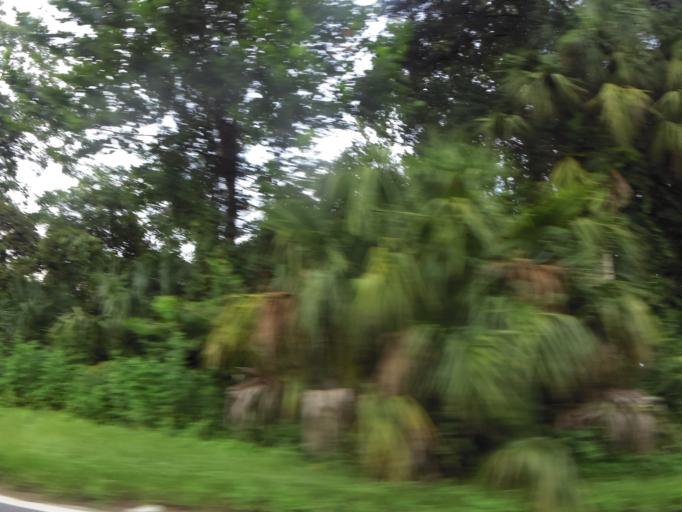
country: US
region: Florida
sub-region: Duval County
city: Jacksonville
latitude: 30.3571
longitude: -81.7178
